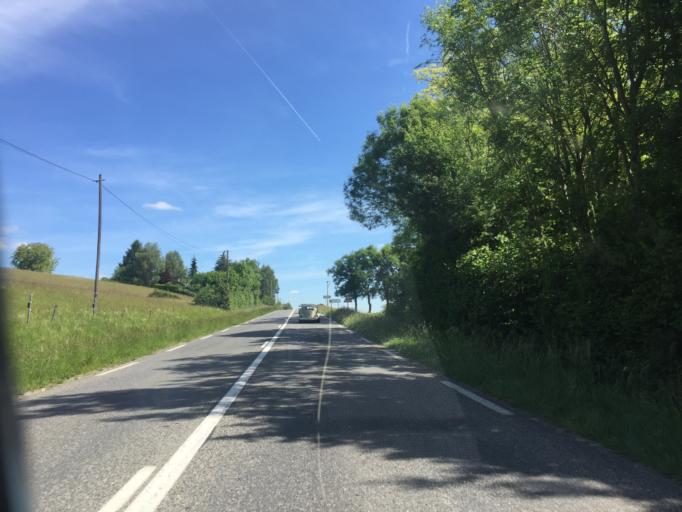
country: FR
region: Rhone-Alpes
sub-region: Departement de la Savoie
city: La Biolle
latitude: 45.7658
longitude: 5.9365
